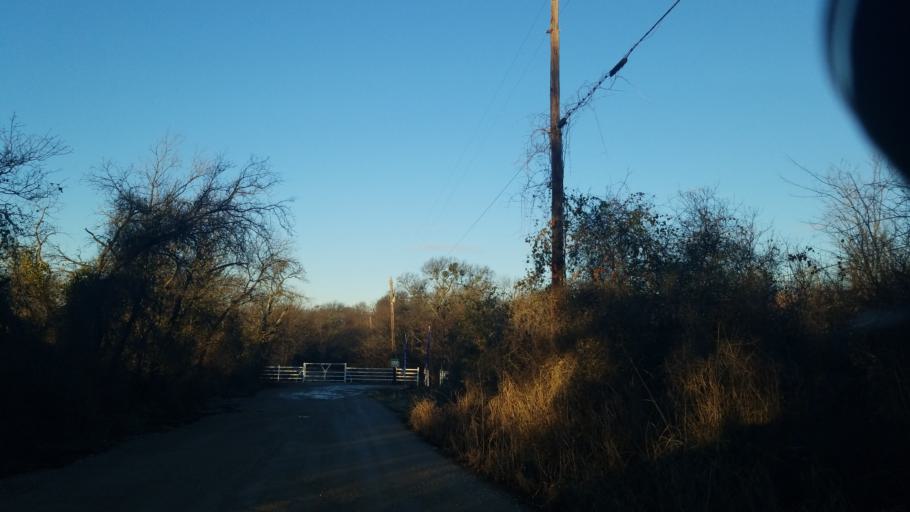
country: US
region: Texas
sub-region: Denton County
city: Justin
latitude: 33.0647
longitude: -97.2479
